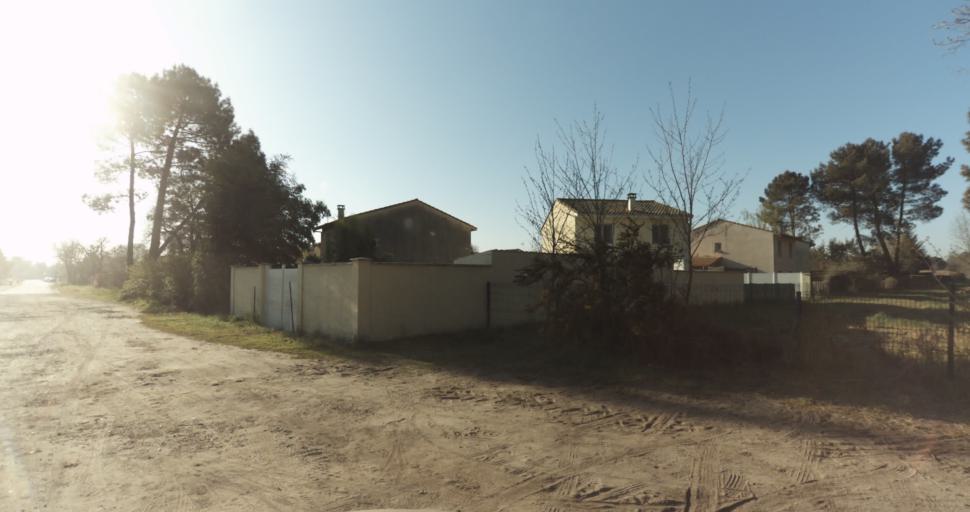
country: FR
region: Aquitaine
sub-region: Departement de la Gironde
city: Martignas-sur-Jalle
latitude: 44.8124
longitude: -0.7989
